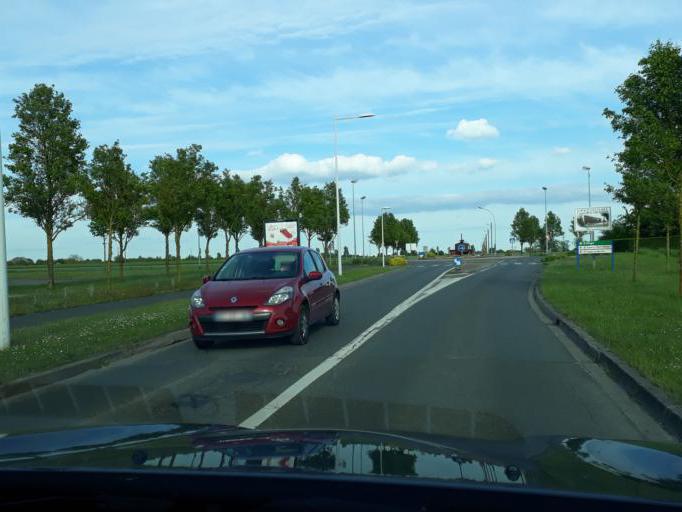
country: FR
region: Centre
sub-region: Departement du Loiret
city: Ingre
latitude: 47.9161
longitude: 1.8391
